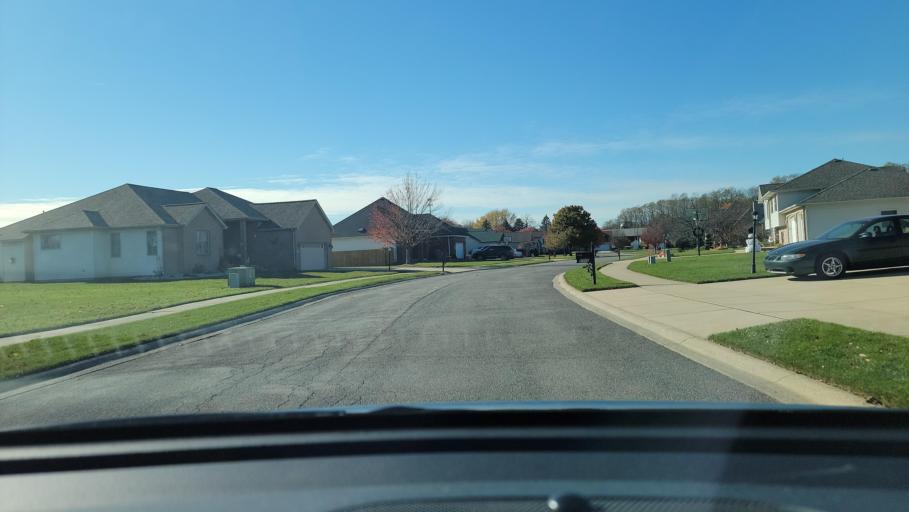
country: US
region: Indiana
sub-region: Porter County
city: Portage
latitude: 41.5766
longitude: -87.1464
